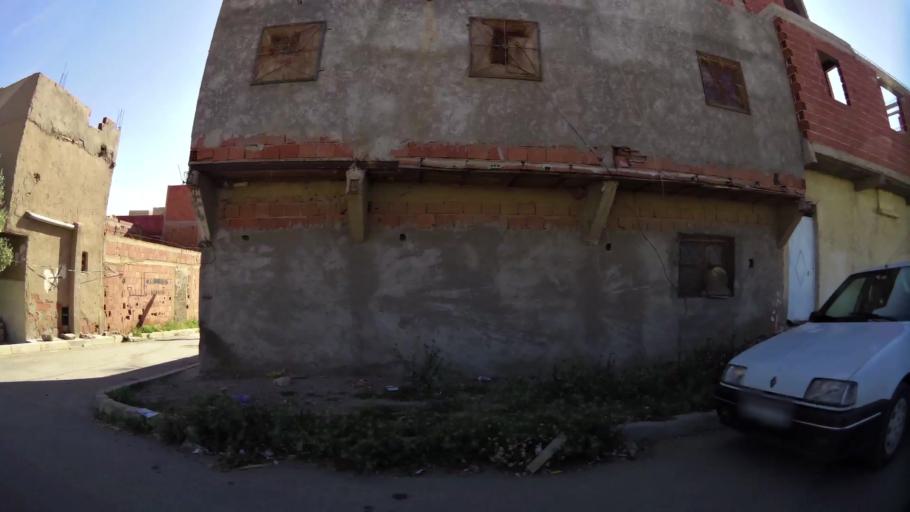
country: MA
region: Oriental
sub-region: Oujda-Angad
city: Oujda
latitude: 34.6557
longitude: -1.9516
